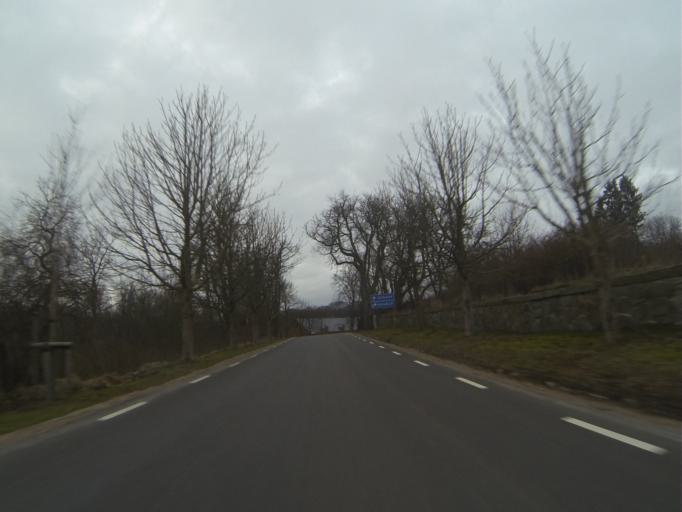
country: SE
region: Skane
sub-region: Lunds Kommun
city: Genarp
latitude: 55.5821
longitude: 13.4304
